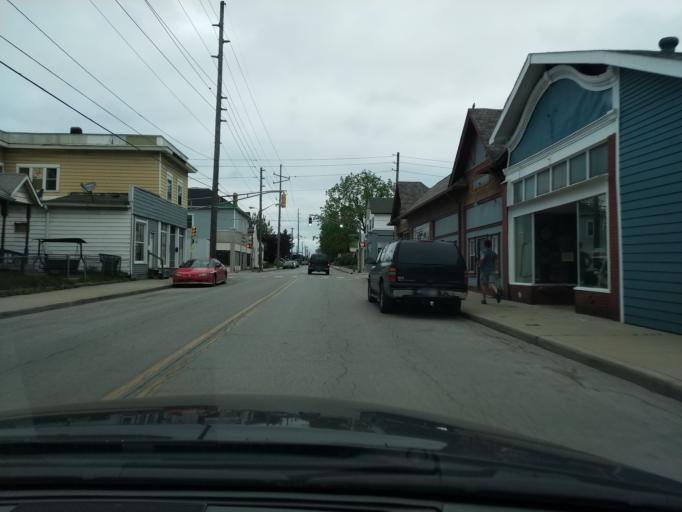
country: US
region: Indiana
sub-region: Marion County
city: Indianapolis
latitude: 39.7452
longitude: -86.1494
